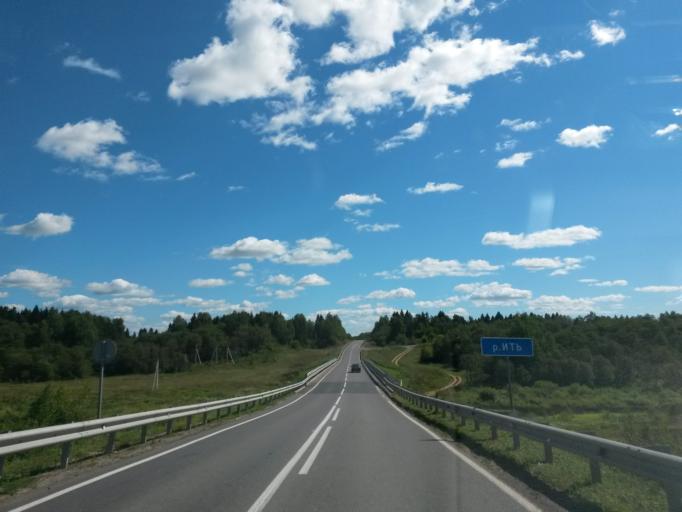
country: RU
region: Jaroslavl
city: Yaroslavl
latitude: 57.7877
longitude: 39.8348
